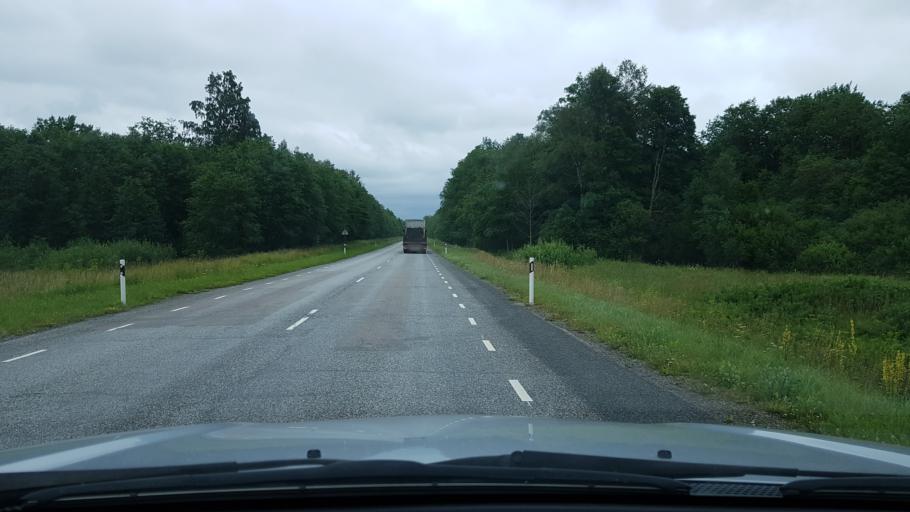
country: EE
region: Ida-Virumaa
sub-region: Narva-Joesuu linn
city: Narva-Joesuu
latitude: 59.3438
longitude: 28.0032
